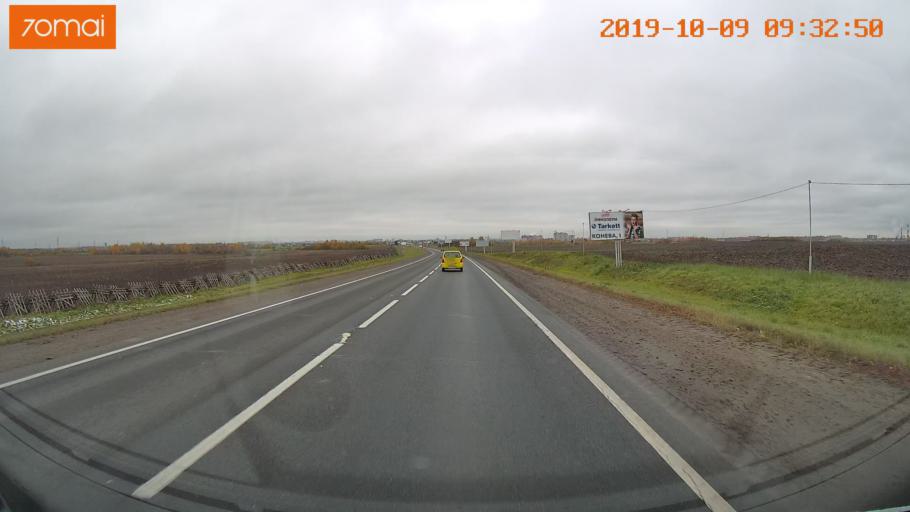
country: RU
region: Vologda
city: Vologda
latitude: 59.1630
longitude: 39.9231
